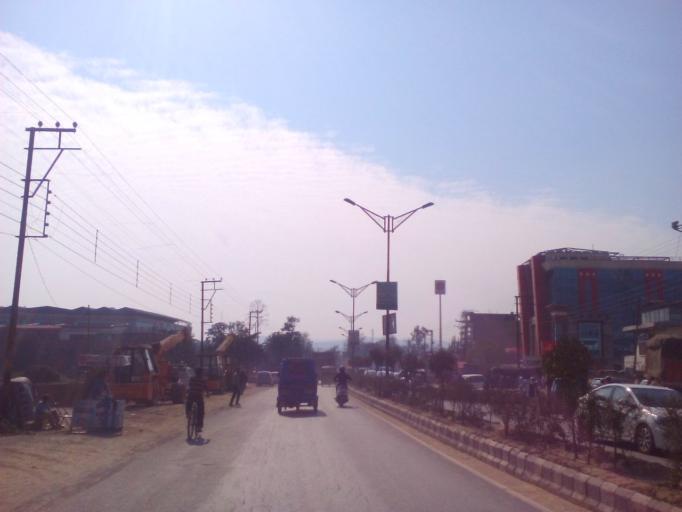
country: IN
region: Uttarakhand
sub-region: Dehradun
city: Clement Town
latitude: 30.2829
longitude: 77.9931
